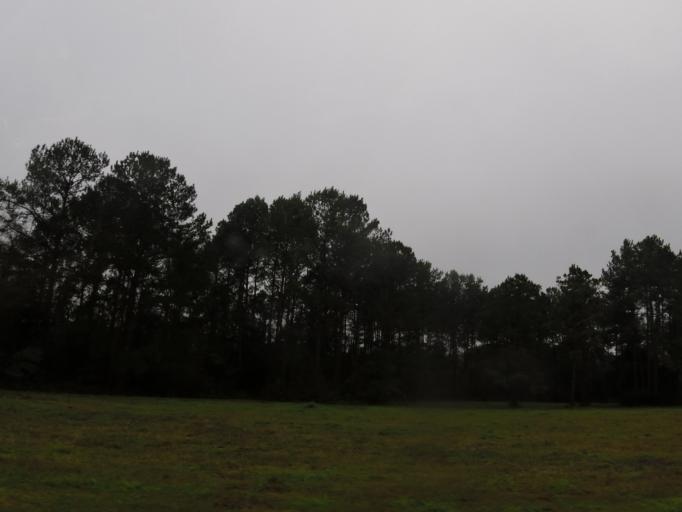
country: US
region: Florida
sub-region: Alachua County
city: High Springs
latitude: 29.8749
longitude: -82.5415
